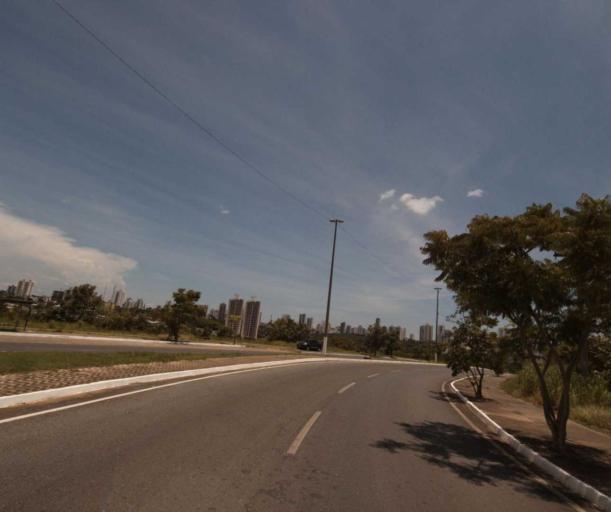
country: BR
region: Mato Grosso
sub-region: Cuiaba
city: Cuiaba
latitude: -15.5685
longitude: -56.1068
